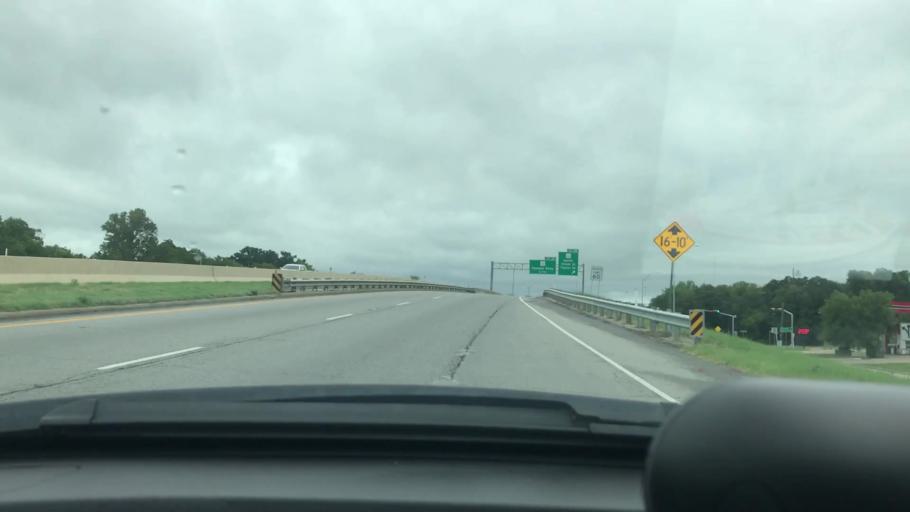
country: US
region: Texas
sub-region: Grayson County
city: Sherman
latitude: 33.6390
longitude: -96.6161
